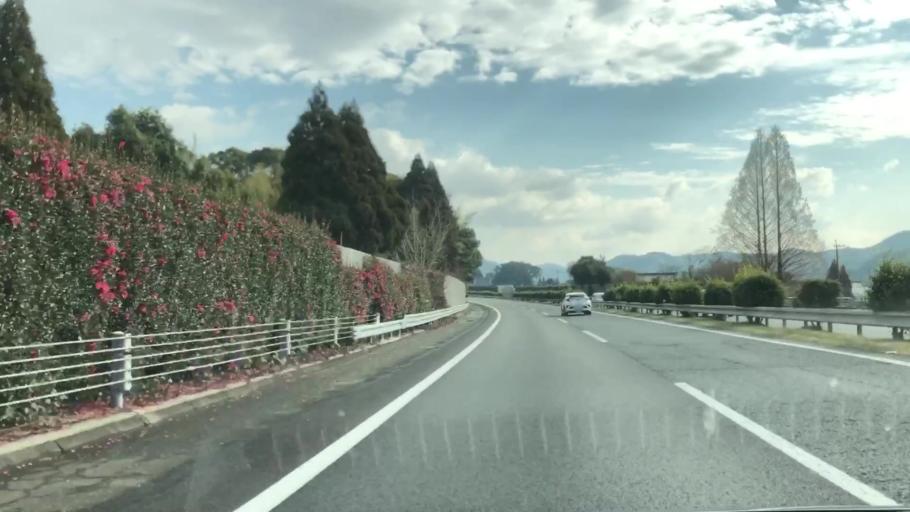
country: JP
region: Fukuoka
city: Setakamachi-takayanagi
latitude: 33.1229
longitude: 130.5198
